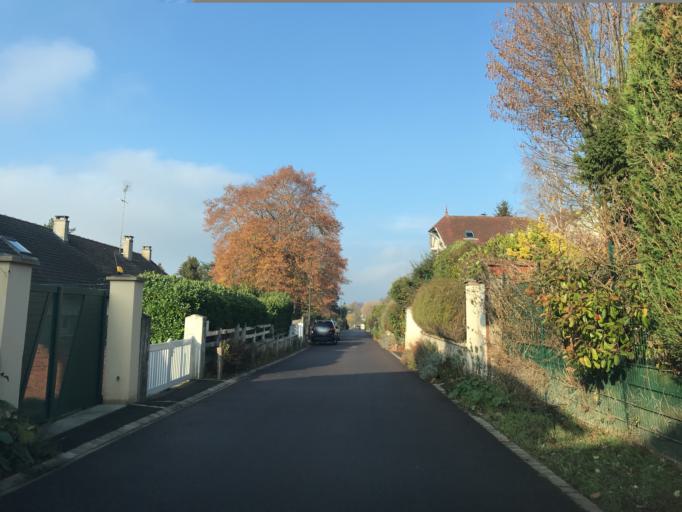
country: FR
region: Ile-de-France
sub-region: Departement des Yvelines
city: Limetz-Villez
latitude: 49.0800
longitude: 1.5191
